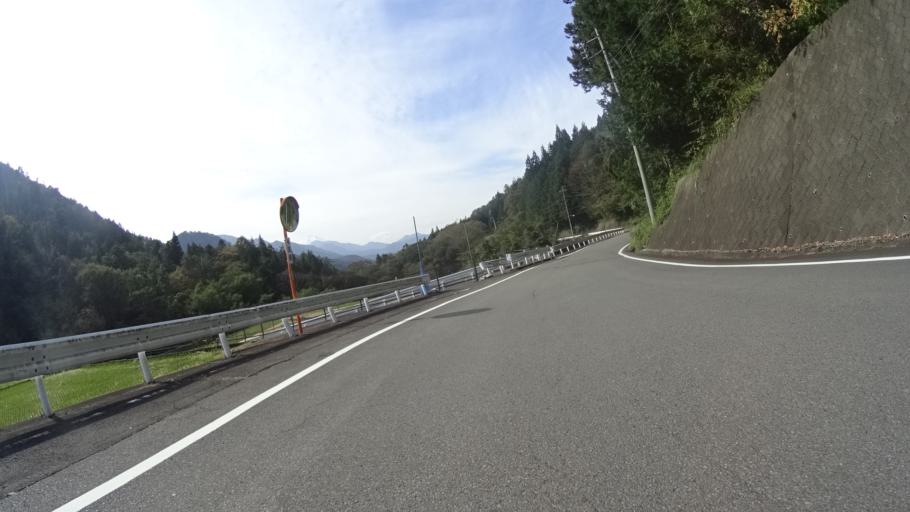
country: JP
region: Yamanashi
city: Otsuki
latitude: 35.5689
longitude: 138.9792
